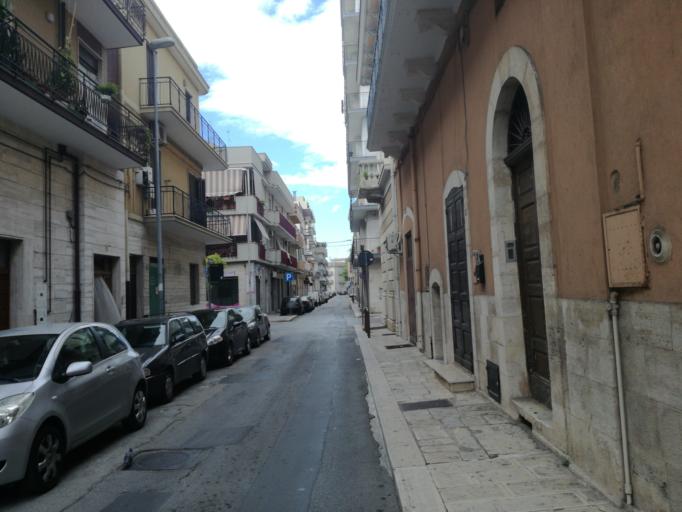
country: IT
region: Apulia
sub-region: Provincia di Bari
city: Triggiano
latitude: 41.0658
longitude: 16.9236
